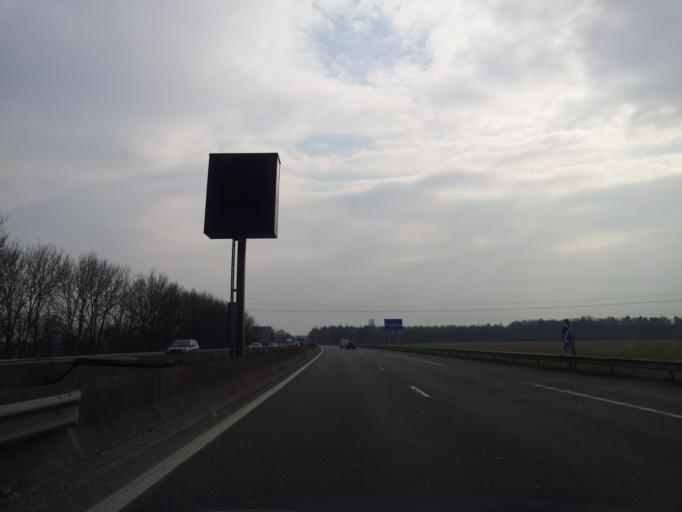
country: FR
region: Alsace
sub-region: Departement du Bas-Rhin
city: Brumath
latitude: 48.7322
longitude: 7.6890
